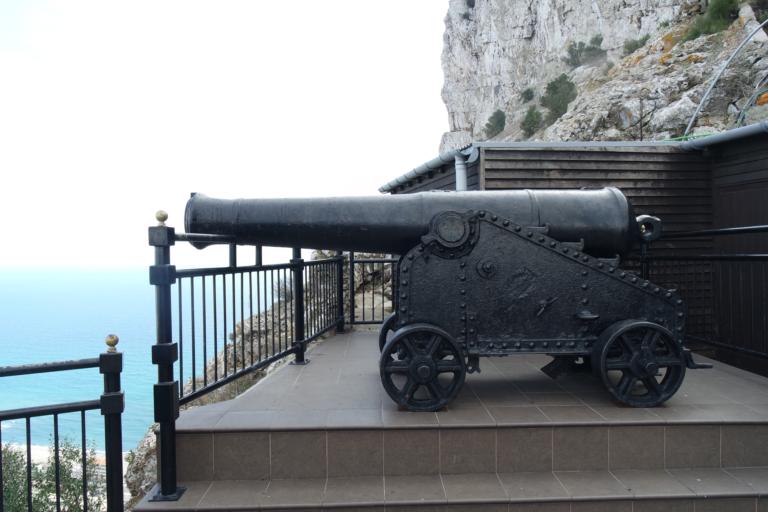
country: GI
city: Gibraltar
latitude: 36.1452
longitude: -5.3451
